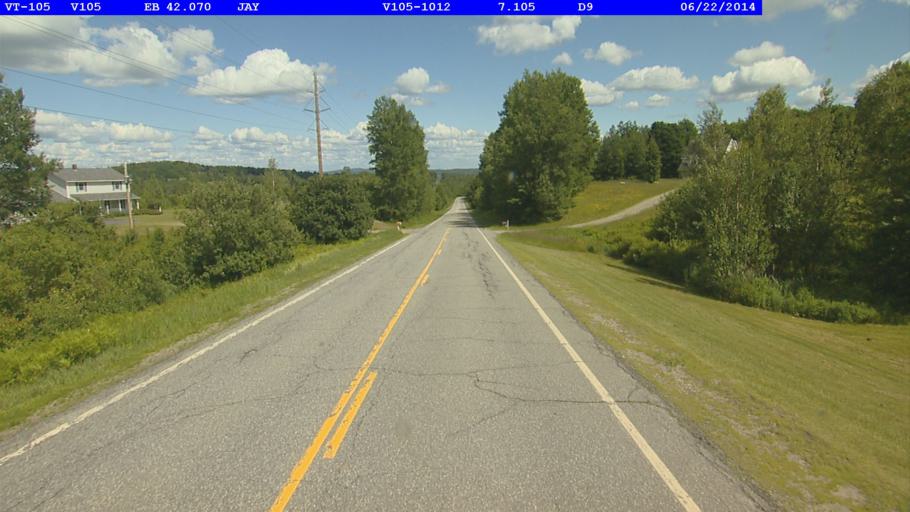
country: CA
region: Quebec
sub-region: Monteregie
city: Sutton
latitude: 44.9694
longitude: -72.4465
